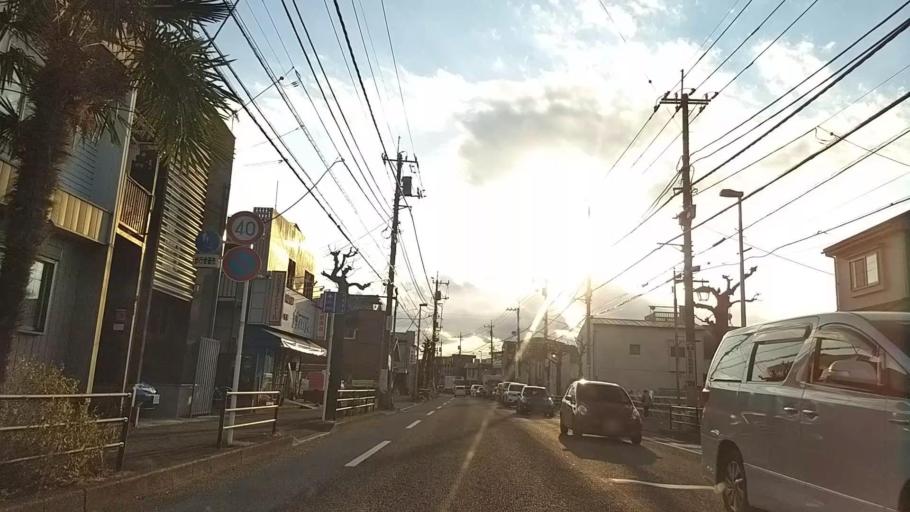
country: JP
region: Kanagawa
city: Atsugi
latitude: 35.4367
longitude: 139.3696
